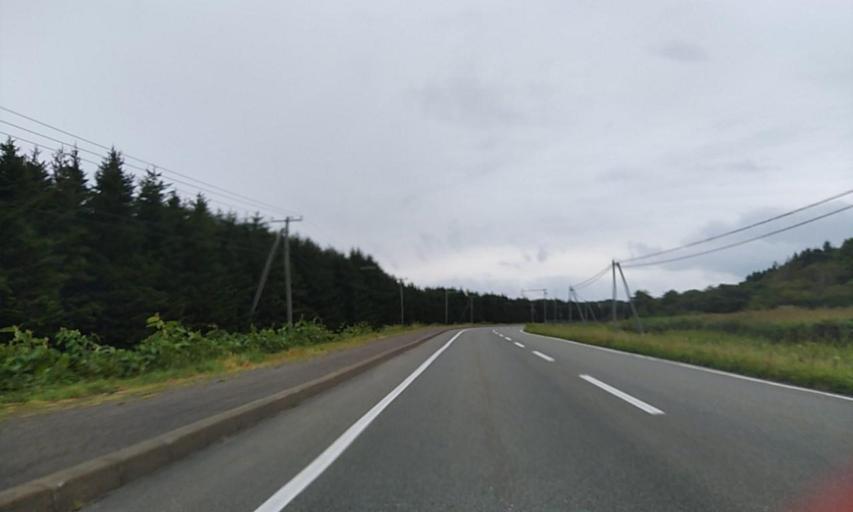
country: JP
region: Hokkaido
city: Nayoro
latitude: 45.0280
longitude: 142.5258
